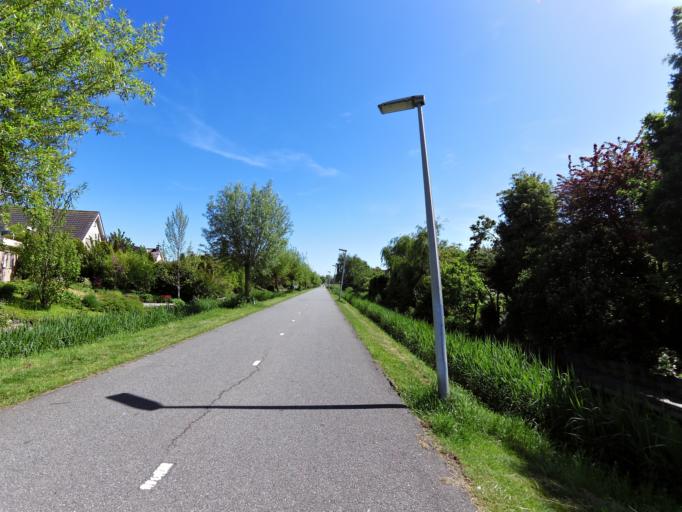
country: NL
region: South Holland
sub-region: Gemeente Hellevoetsluis
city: Nieuwenhoorn
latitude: 51.8431
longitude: 4.1597
